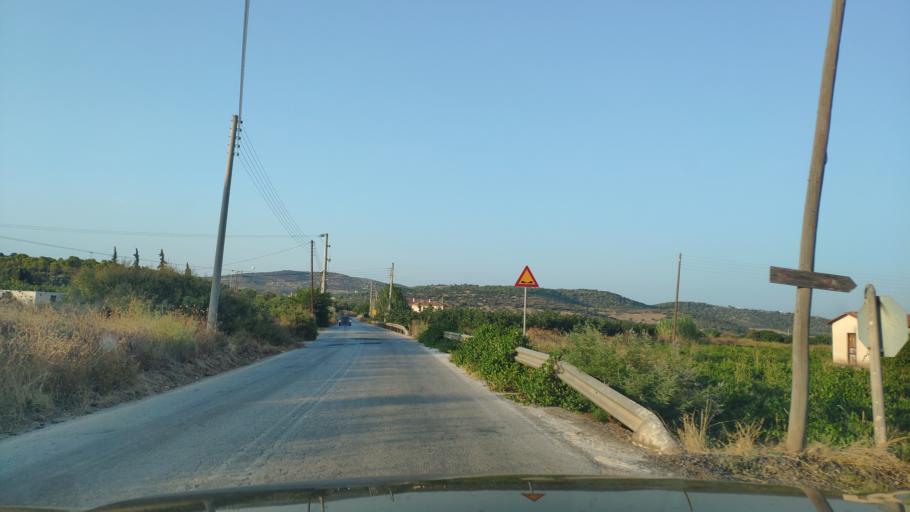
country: GR
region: Attica
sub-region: Nomarchia Anatolikis Attikis
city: Limin Mesoyaias
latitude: 37.9183
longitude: 23.9757
